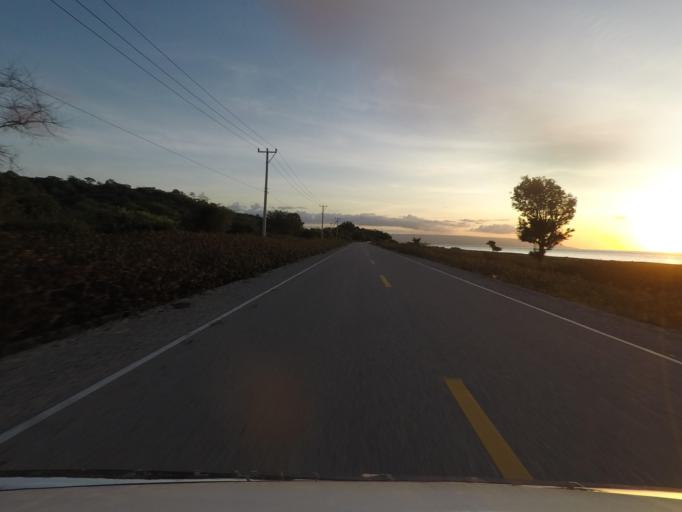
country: TL
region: Baucau
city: Baucau
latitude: -8.4581
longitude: 126.6157
